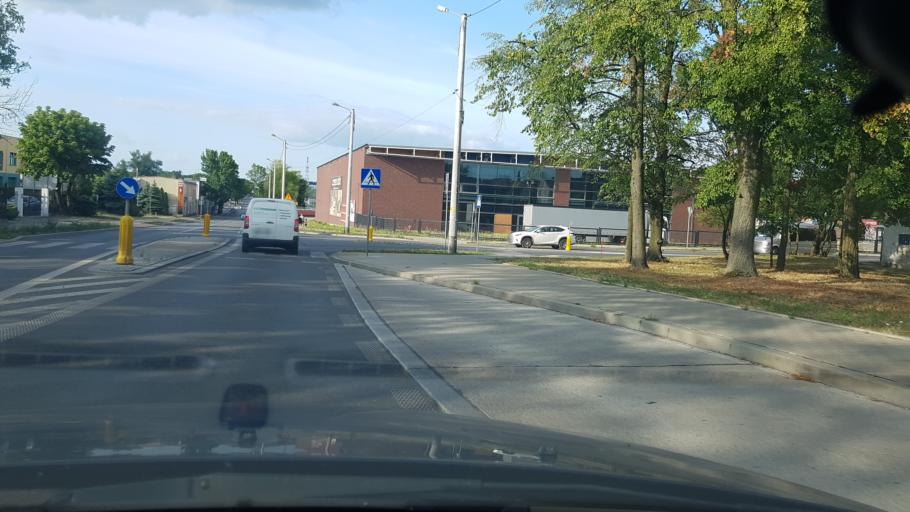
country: PL
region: Lodz Voivodeship
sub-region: Powiat tomaszowski
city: Tomaszow Mazowiecki
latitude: 51.5475
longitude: 20.0149
